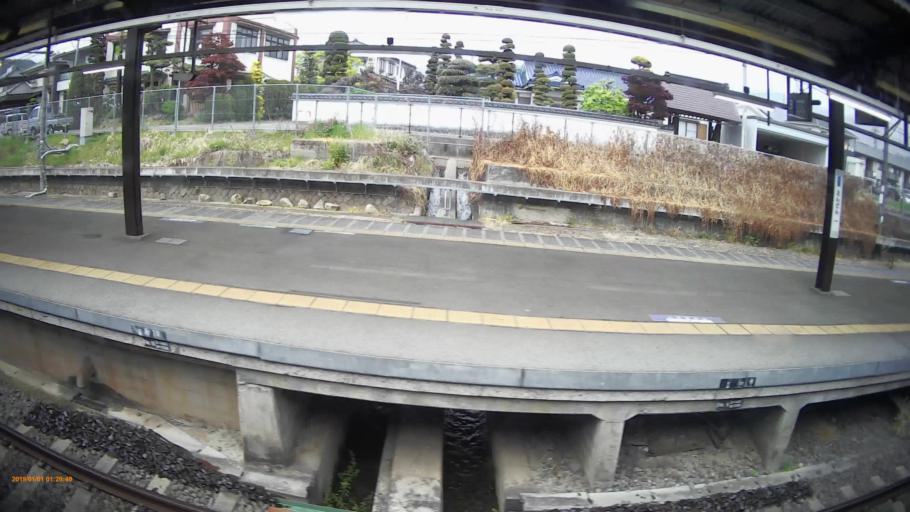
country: JP
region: Yamanashi
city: Enzan
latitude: 35.7053
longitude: 138.7356
